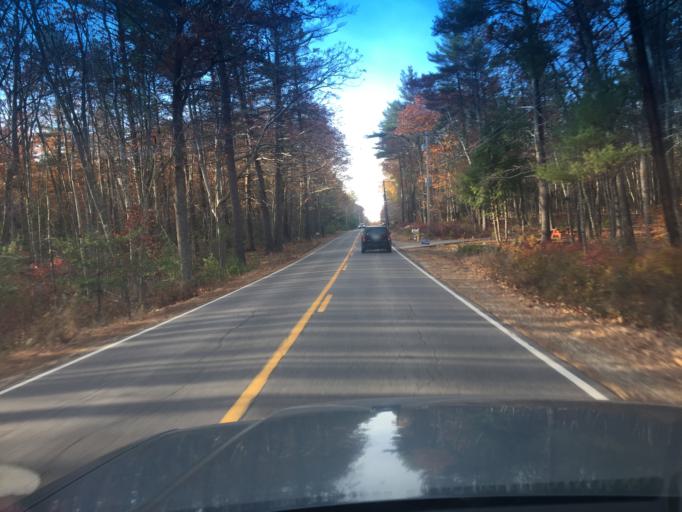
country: US
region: Maine
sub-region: York County
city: Eliot
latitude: 43.1884
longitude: -70.7469
